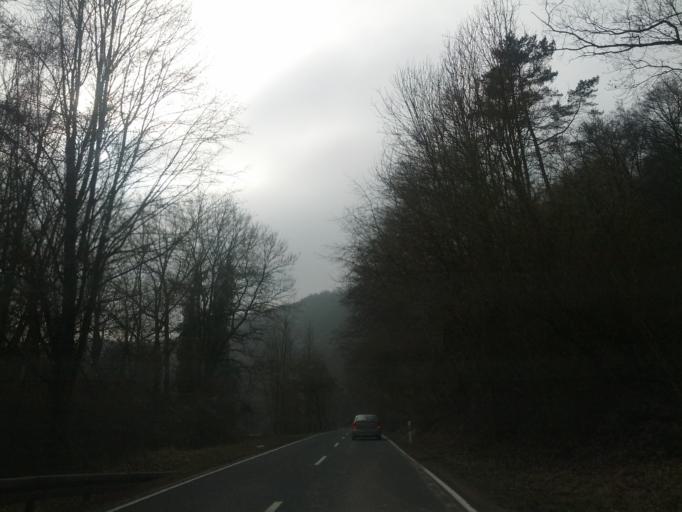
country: DE
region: Thuringia
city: Creuzburg
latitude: 51.0732
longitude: 10.2689
